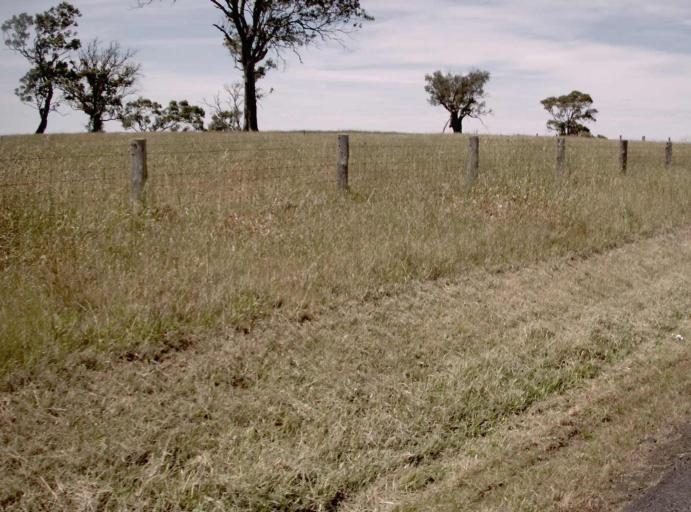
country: AU
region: Victoria
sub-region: Latrobe
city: Traralgon
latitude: -38.1764
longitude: 146.6439
